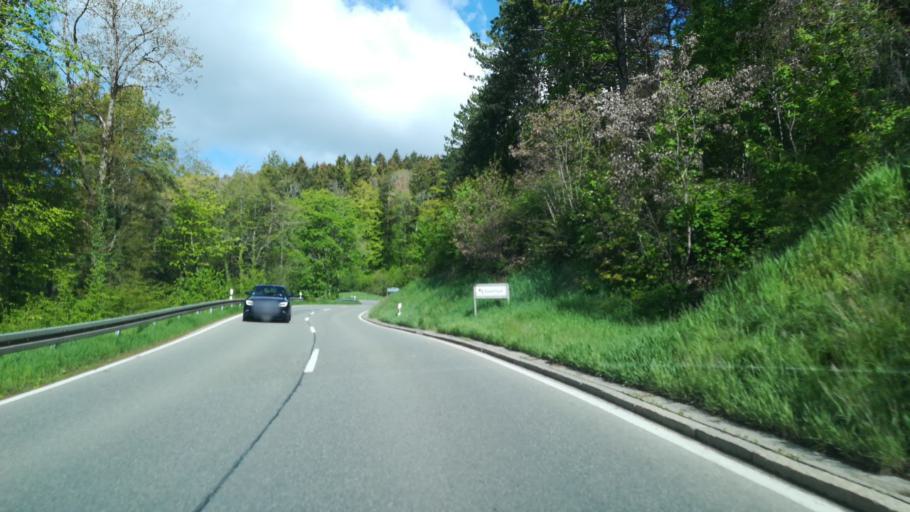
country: DE
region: Baden-Wuerttemberg
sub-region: Freiburg Region
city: Tengen
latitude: 47.8245
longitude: 8.6380
